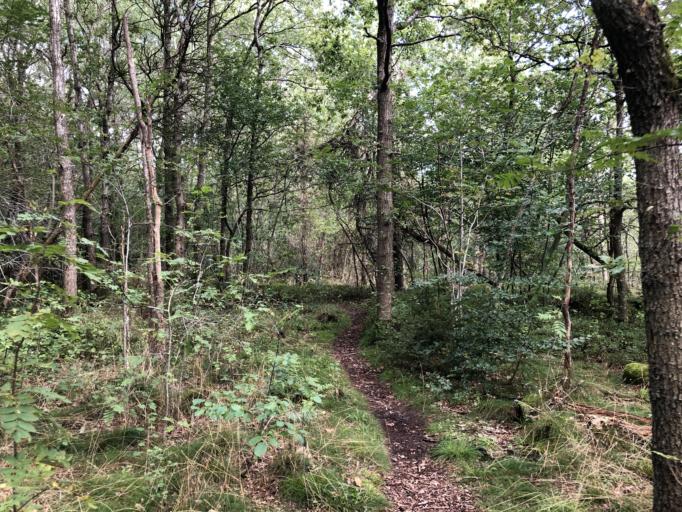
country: DK
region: Central Jutland
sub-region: Holstebro Kommune
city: Ulfborg
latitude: 56.3844
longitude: 8.3647
